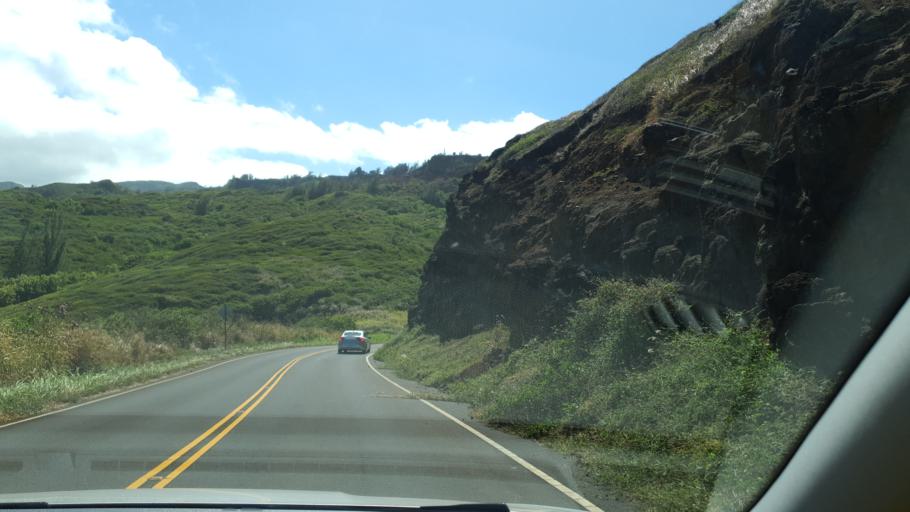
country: US
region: Hawaii
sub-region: Maui County
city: Napili-Honokowai
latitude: 21.0133
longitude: -156.5709
